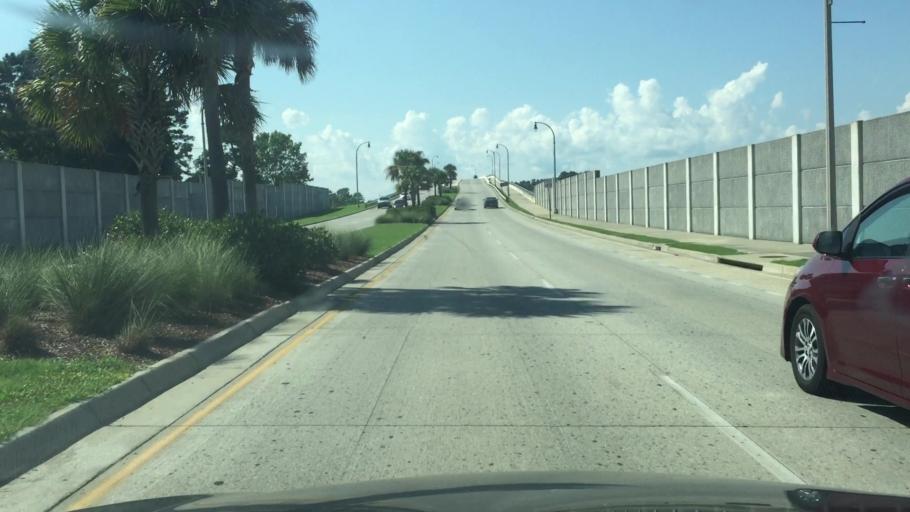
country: US
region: South Carolina
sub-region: Horry County
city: North Myrtle Beach
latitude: 33.8306
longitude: -78.6816
